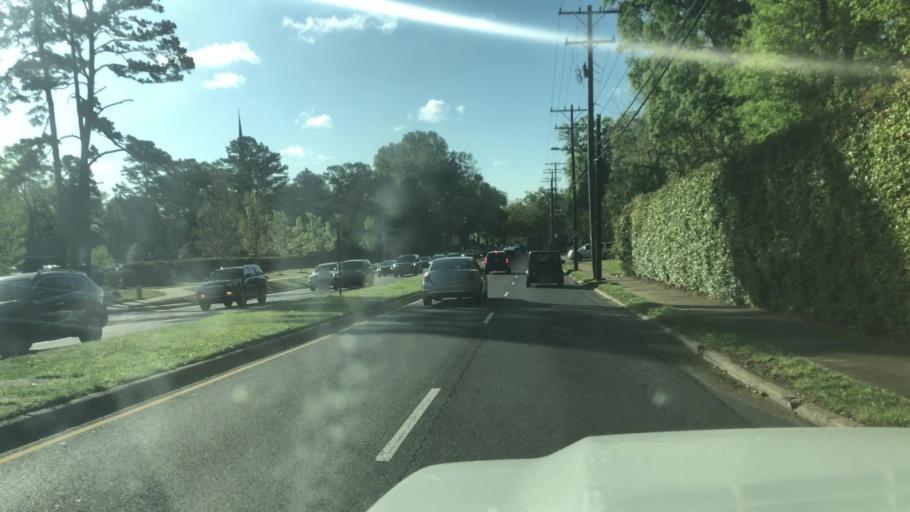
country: US
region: North Carolina
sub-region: Mecklenburg County
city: Charlotte
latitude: 35.1697
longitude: -80.8065
